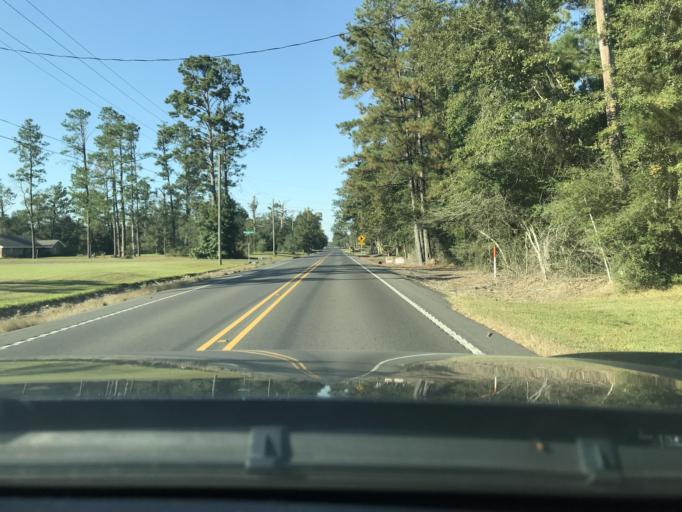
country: US
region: Louisiana
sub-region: Calcasieu Parish
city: Moss Bluff
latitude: 30.3375
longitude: -93.2580
